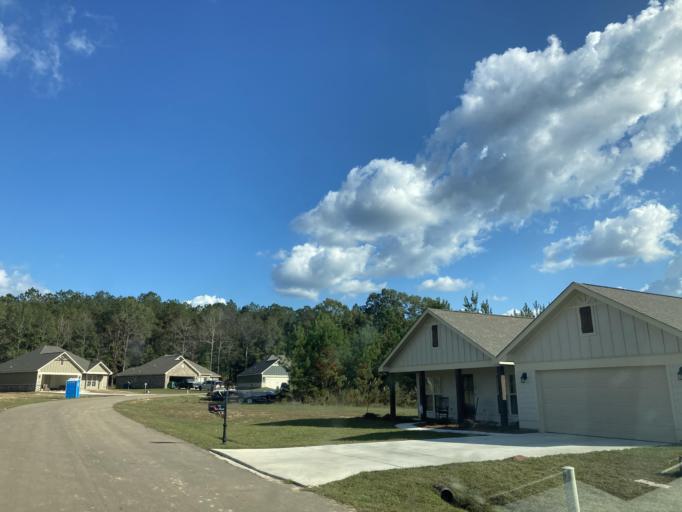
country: US
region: Mississippi
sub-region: Lamar County
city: Sumrall
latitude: 31.4301
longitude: -89.5333
